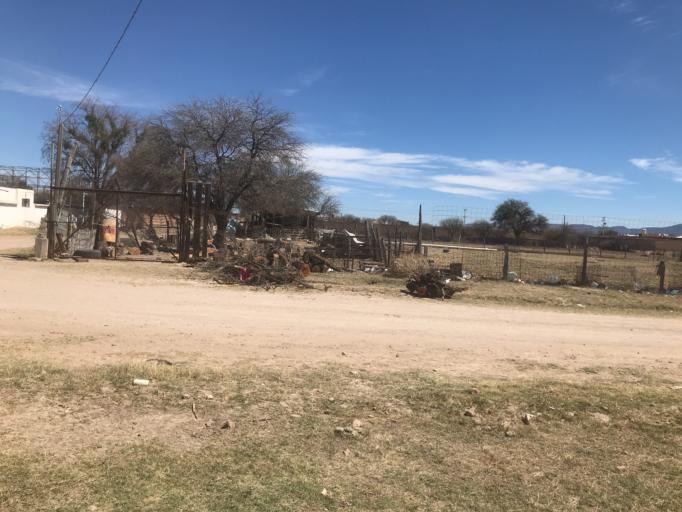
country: MX
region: Durango
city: Victoria de Durango
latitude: 24.0157
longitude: -104.5919
